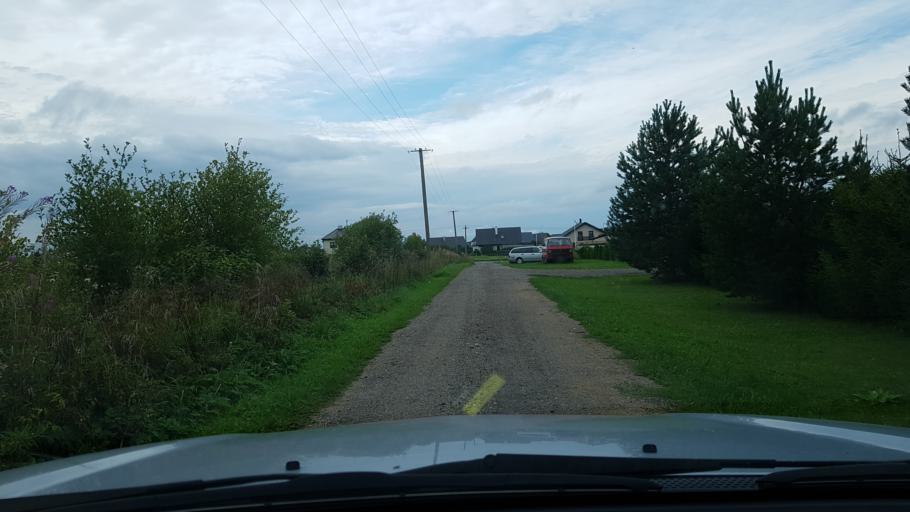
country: EE
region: Harju
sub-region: Joelaehtme vald
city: Loo
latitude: 59.4092
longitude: 24.9583
